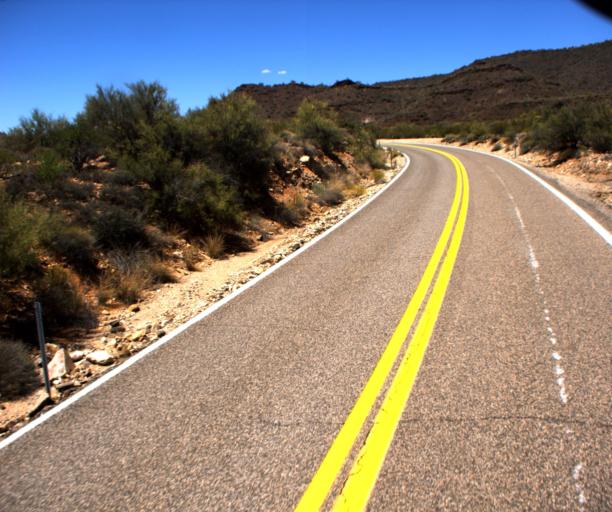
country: US
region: Arizona
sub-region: Yavapai County
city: Bagdad
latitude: 34.4931
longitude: -113.0641
